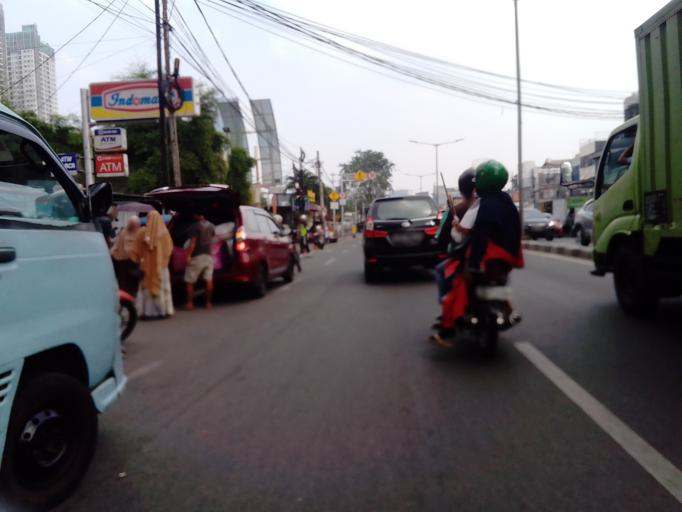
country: ID
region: Jakarta Raya
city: Jakarta
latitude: -6.1944
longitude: 106.8145
